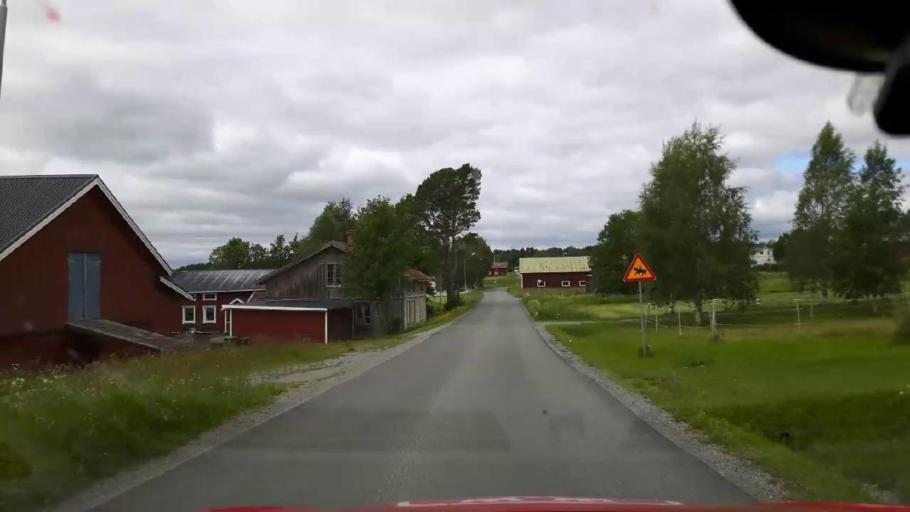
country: SE
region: Jaemtland
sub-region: OEstersunds Kommun
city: Brunflo
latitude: 63.0783
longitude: 14.8763
